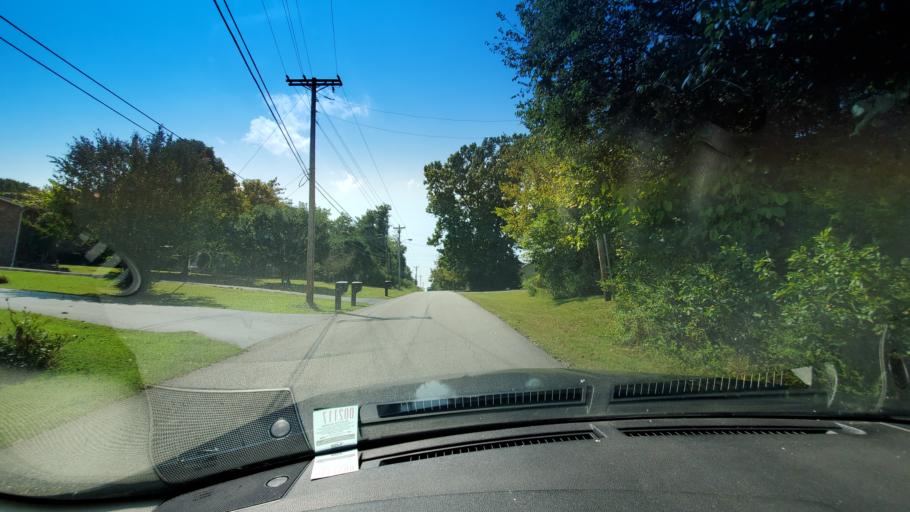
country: US
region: Tennessee
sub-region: Smith County
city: Carthage
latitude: 36.2533
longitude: -85.9621
